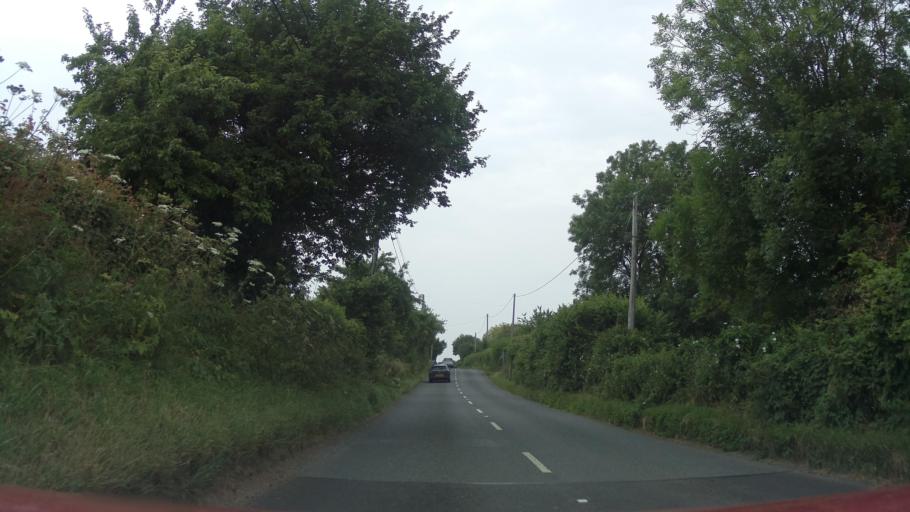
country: GB
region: England
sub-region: Somerset
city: Crewkerne
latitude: 50.8875
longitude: -2.7482
